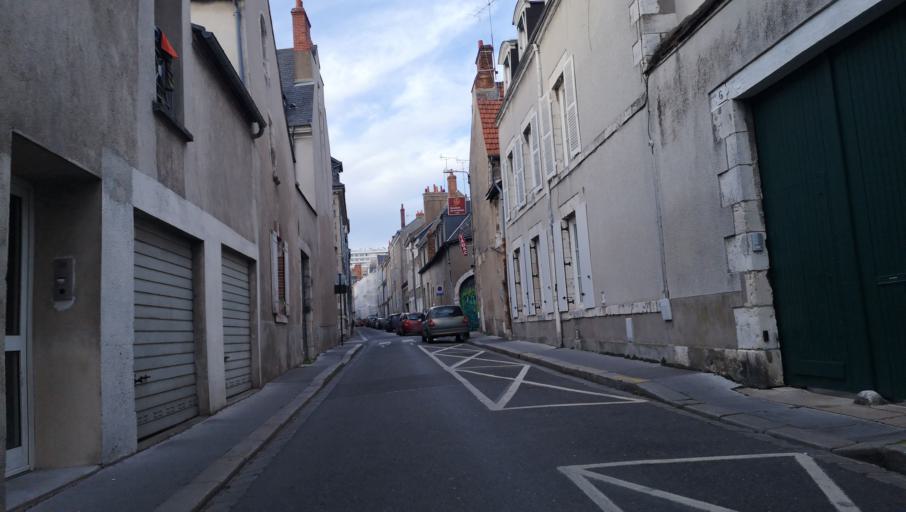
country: FR
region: Centre
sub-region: Departement du Loiret
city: Orleans
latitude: 47.9039
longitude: 1.9010
